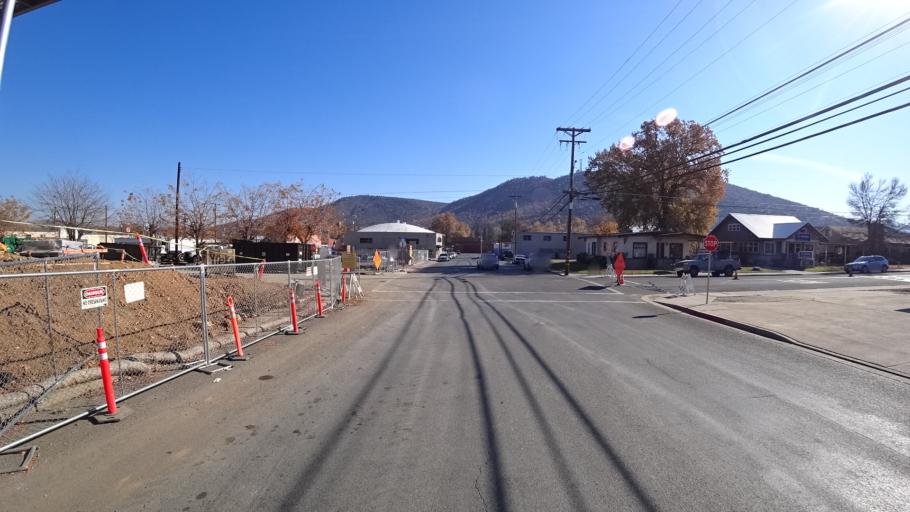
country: US
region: California
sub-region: Siskiyou County
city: Yreka
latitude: 41.7288
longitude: -122.6388
